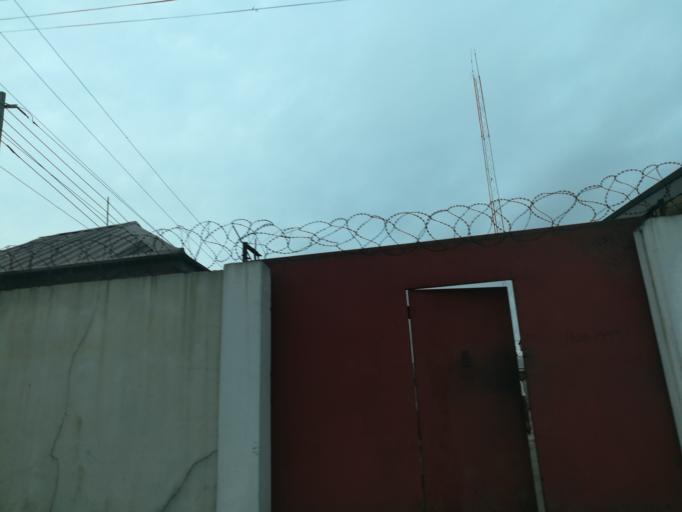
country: NG
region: Rivers
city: Port Harcourt
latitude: 4.8186
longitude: 7.0259
